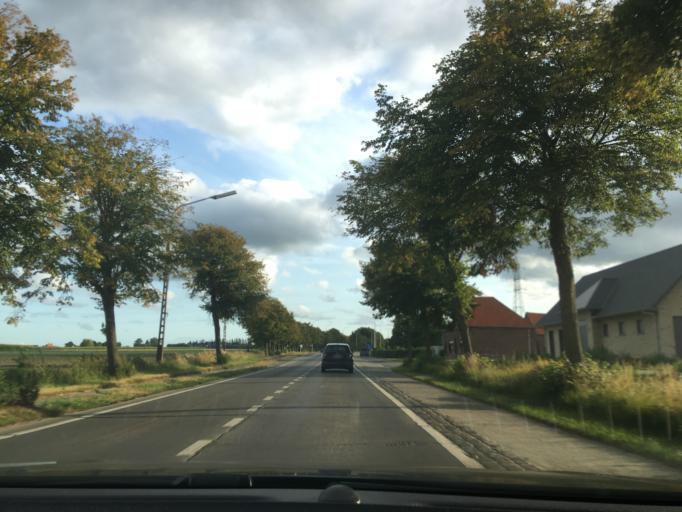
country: BE
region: Flanders
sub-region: Provincie West-Vlaanderen
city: Ieper
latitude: 50.8811
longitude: 2.9278
